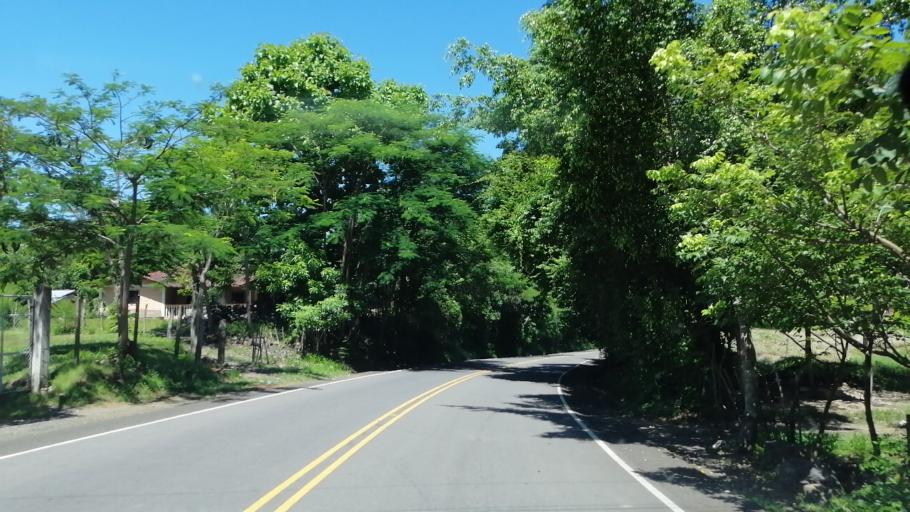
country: SV
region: Morazan
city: Cacaopera
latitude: 13.8144
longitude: -88.1716
